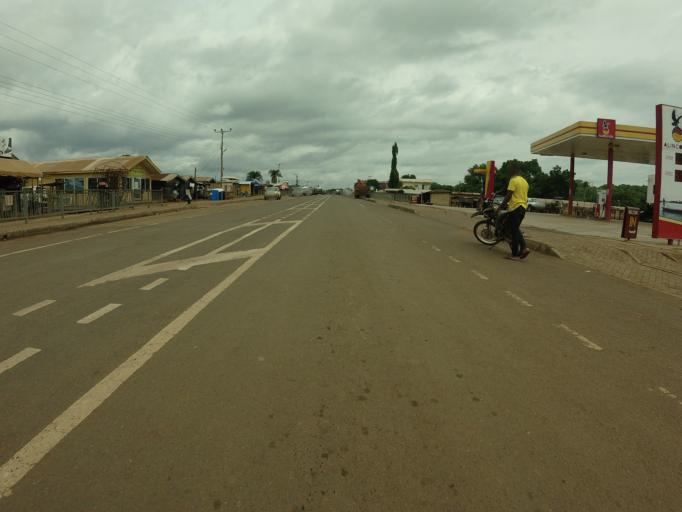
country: TG
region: Centrale
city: Sotouboua
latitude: 8.2642
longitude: 0.5205
